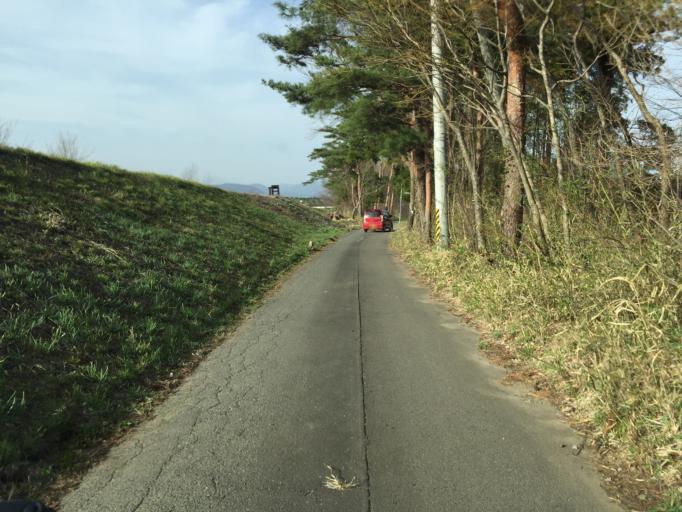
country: JP
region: Fukushima
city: Fukushima-shi
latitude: 37.7242
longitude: 140.3714
